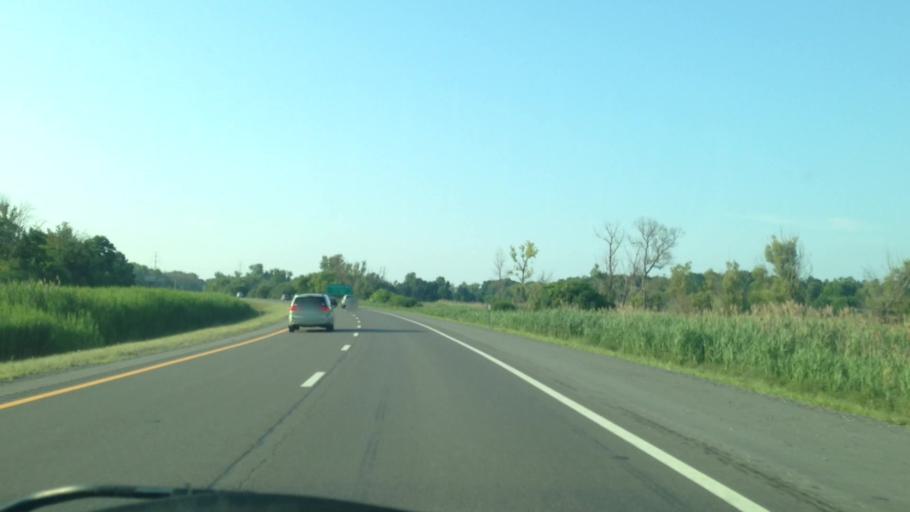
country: US
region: New York
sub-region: Onondaga County
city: East Syracuse
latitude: 43.0216
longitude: -76.0622
